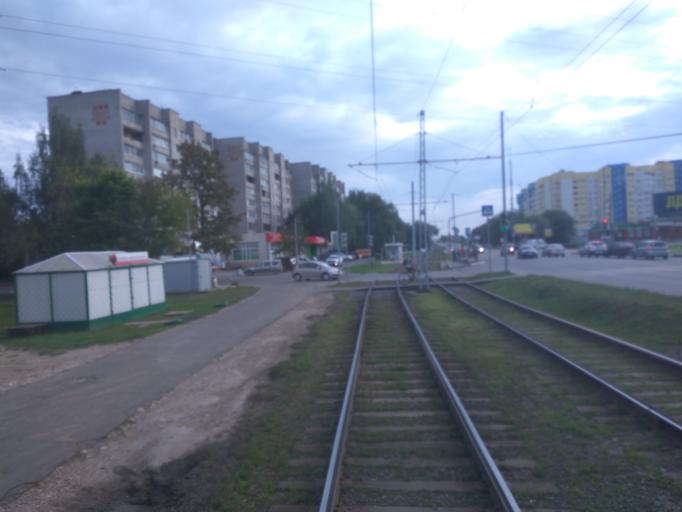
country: RU
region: Moskovskaya
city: Kolomna
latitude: 55.0777
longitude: 38.7620
